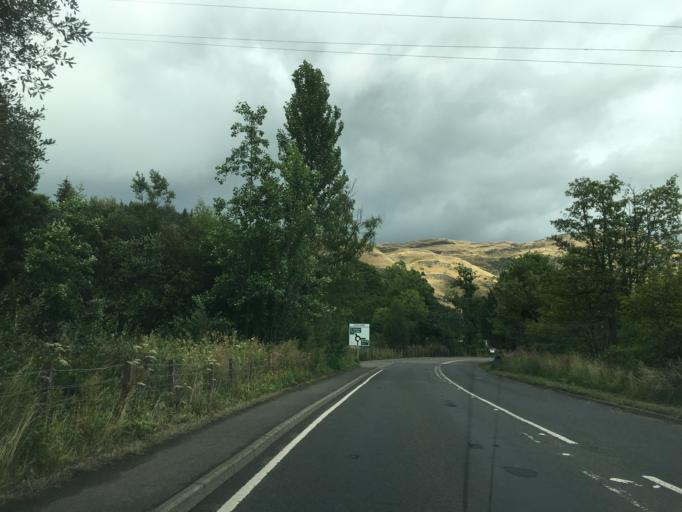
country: GB
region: Scotland
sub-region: Stirling
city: Bridge of Allan
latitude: 56.1462
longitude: -3.9060
